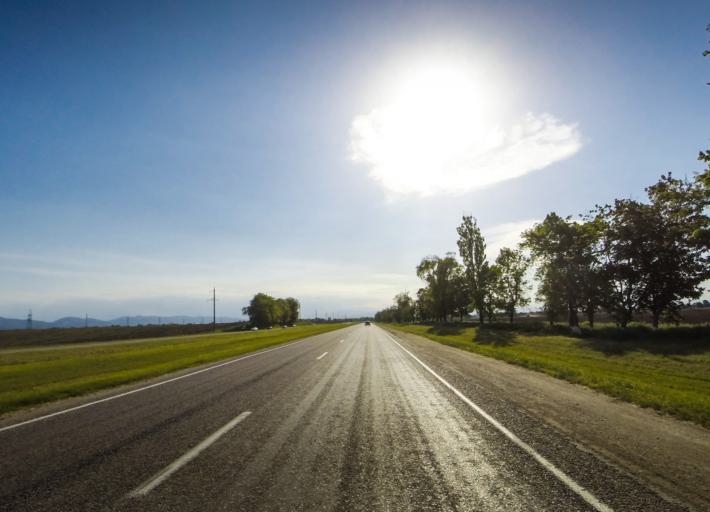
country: RU
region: Kabardino-Balkariya
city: Urvan'
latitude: 43.5041
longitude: 43.7336
